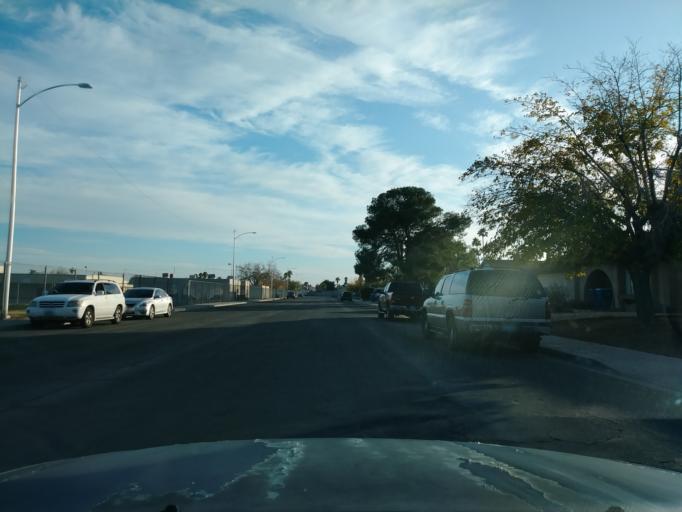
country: US
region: Nevada
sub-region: Clark County
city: Spring Valley
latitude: 36.1709
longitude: -115.2354
